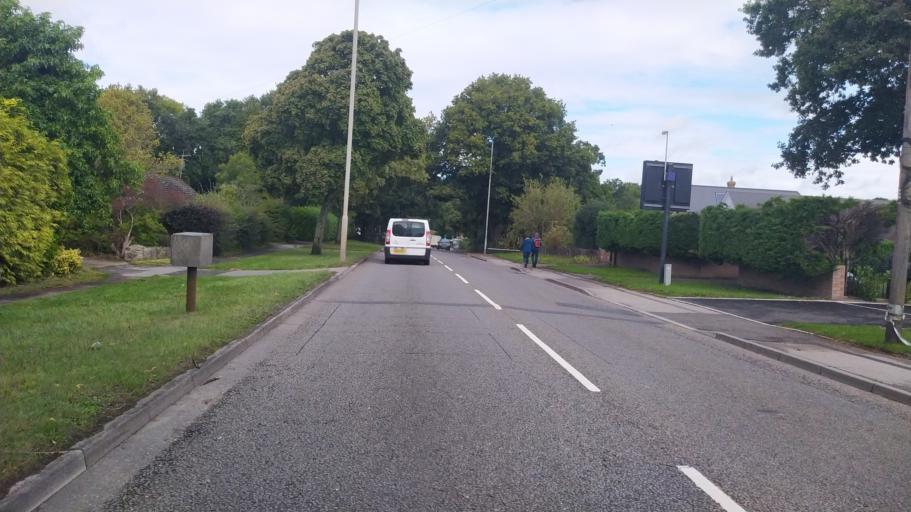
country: GB
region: England
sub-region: Dorset
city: Wimborne Minster
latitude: 50.7817
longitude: -1.9785
